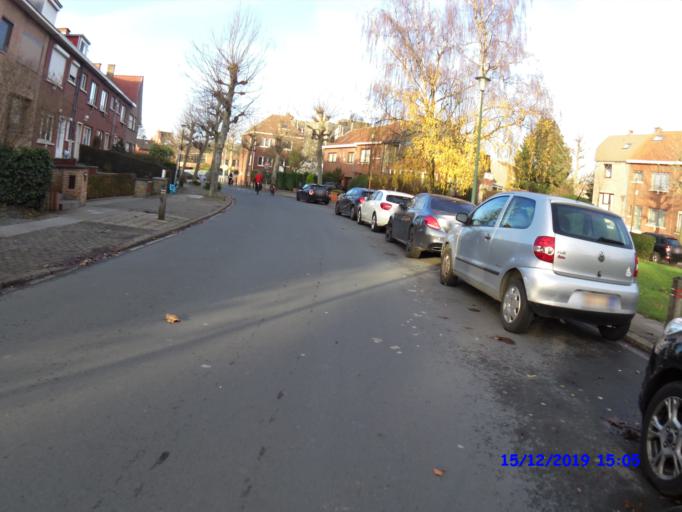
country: BE
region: Flanders
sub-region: Provincie Vlaams-Brabant
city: Drogenbos
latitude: 50.7861
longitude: 4.3267
